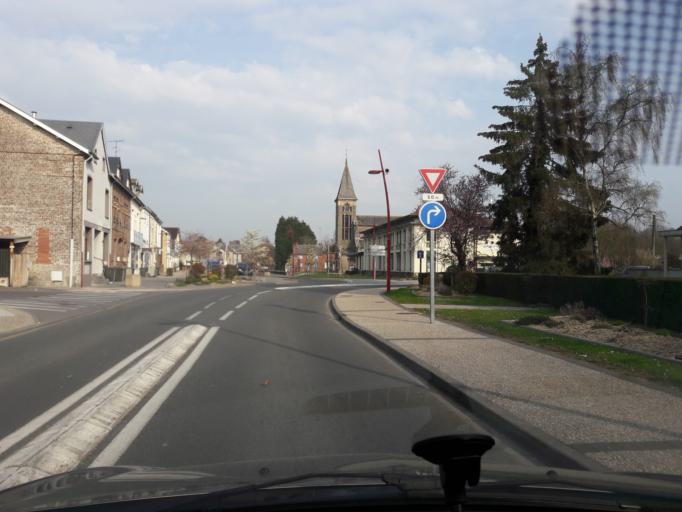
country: FR
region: Nord-Pas-de-Calais
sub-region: Departement du Nord
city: Boussois
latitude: 50.2891
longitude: 4.0390
